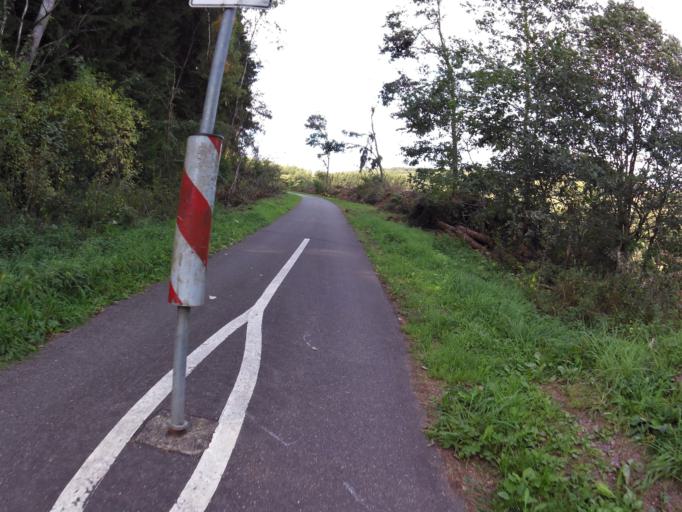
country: DE
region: Rheinland-Pfalz
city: Bleialf
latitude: 50.2107
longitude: 6.2826
